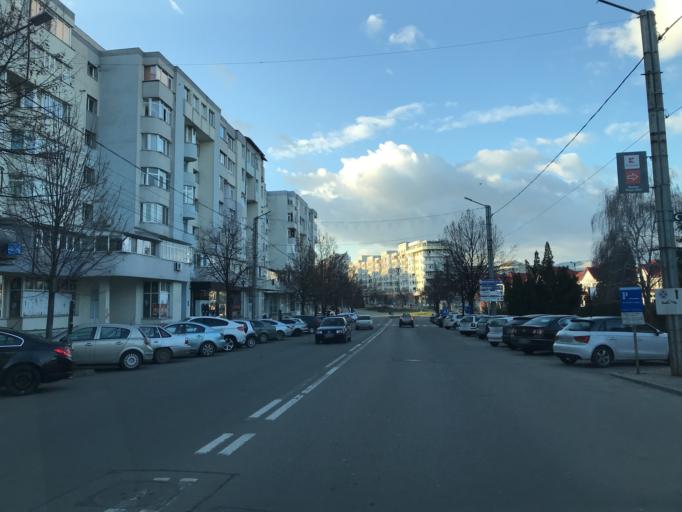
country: RO
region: Olt
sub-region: Municipiul Slatina
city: Slatina
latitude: 44.4254
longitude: 24.3771
